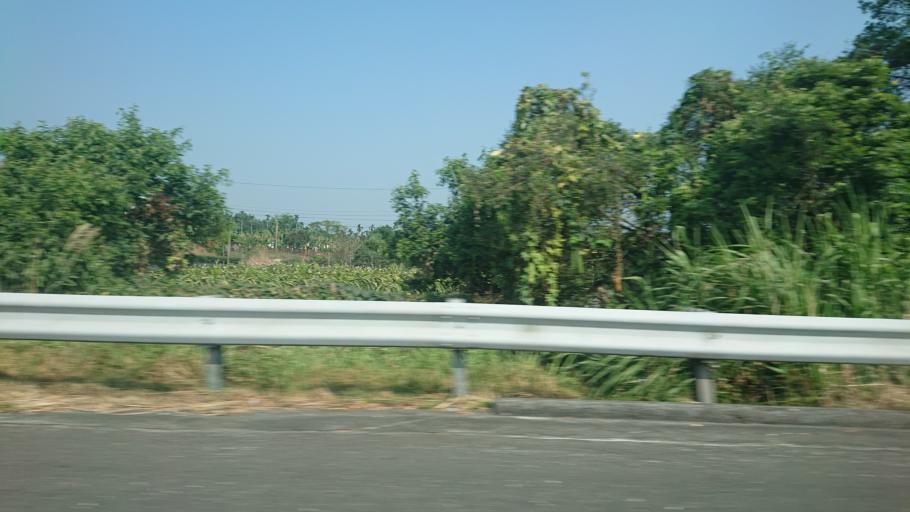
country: TW
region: Taiwan
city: Lugu
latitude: 23.7772
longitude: 120.6924
